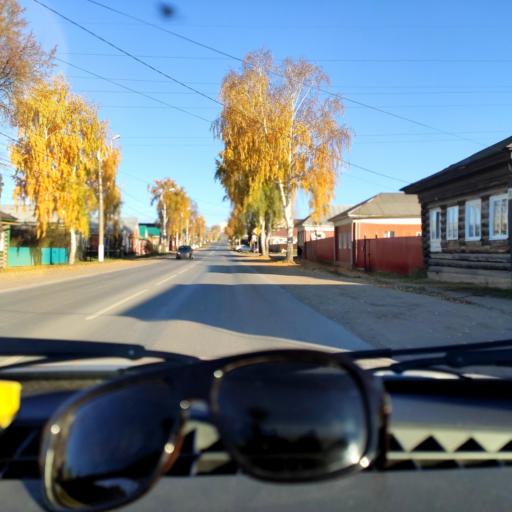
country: RU
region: Bashkortostan
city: Blagoveshchensk
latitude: 55.0372
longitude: 55.9637
